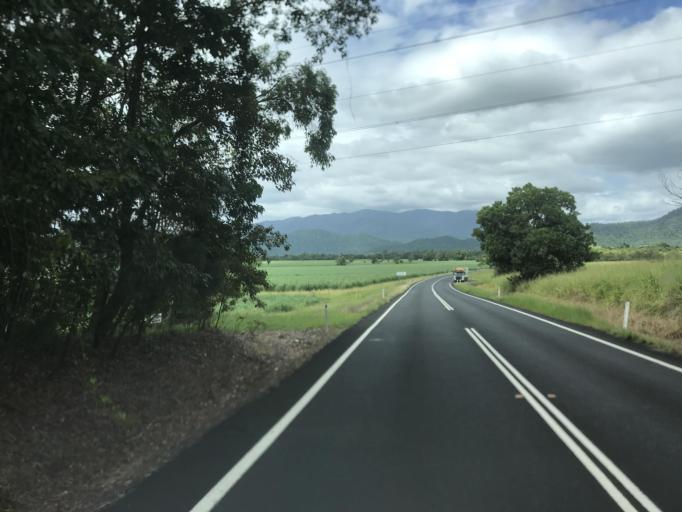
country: AU
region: Queensland
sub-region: Cassowary Coast
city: Innisfail
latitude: -17.8111
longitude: 146.0265
